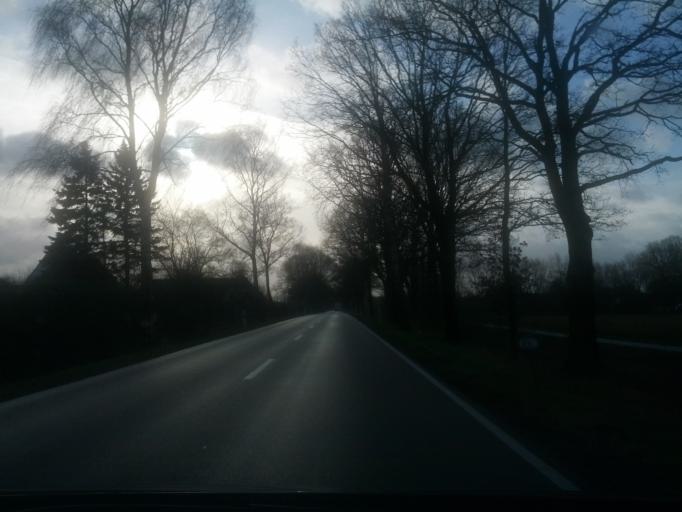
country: DE
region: Lower Saxony
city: Helvesiek
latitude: 53.2317
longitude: 9.4844
